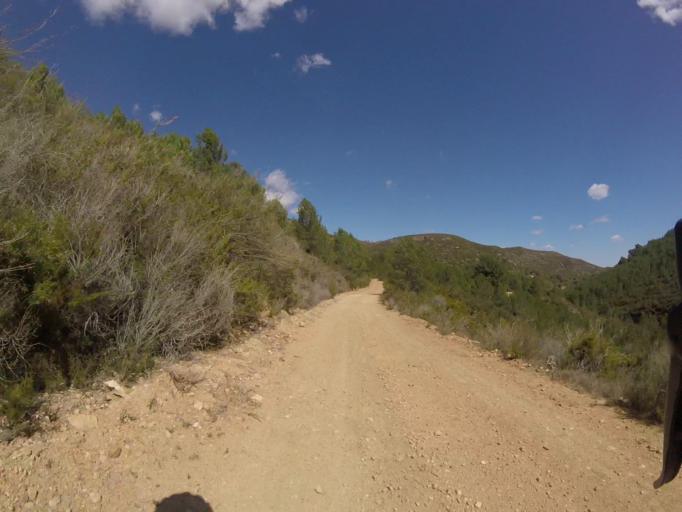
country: ES
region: Valencia
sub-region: Provincia de Castello
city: Cabanes
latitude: 40.1625
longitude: 0.1133
